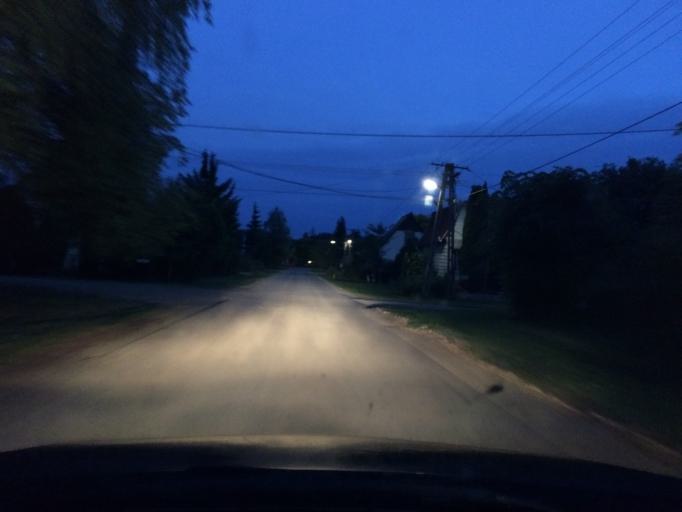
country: HU
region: Szabolcs-Szatmar-Bereg
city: Tiszavasvari
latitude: 47.9558
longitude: 21.3471
